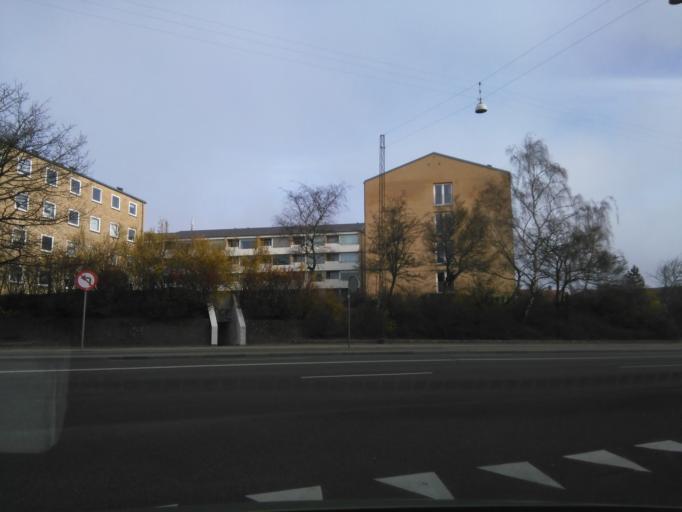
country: DK
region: Central Jutland
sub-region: Arhus Kommune
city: Arhus
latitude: 56.1740
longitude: 10.2138
